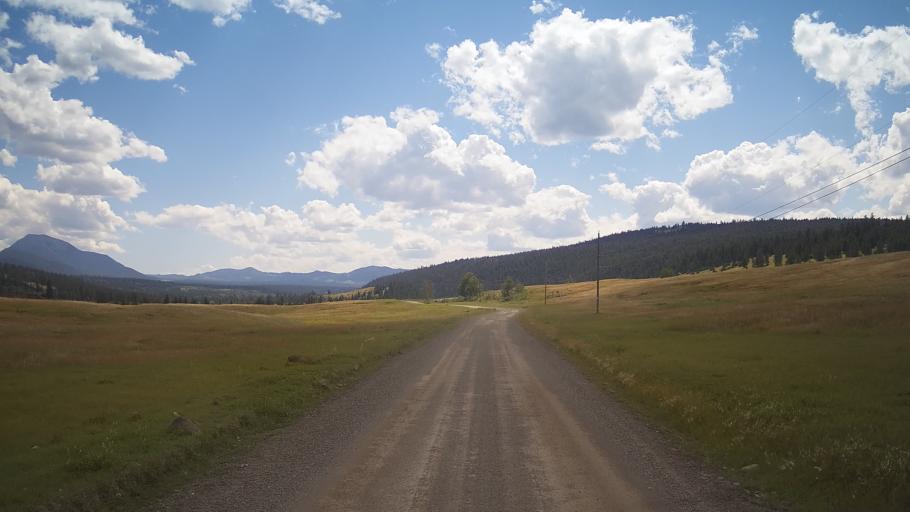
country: CA
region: British Columbia
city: Lillooet
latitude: 51.3130
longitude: -121.9838
